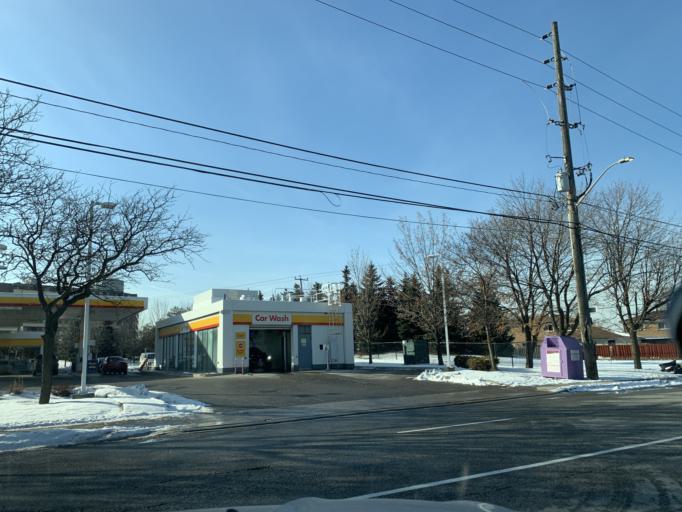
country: CA
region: Ontario
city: Etobicoke
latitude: 43.7166
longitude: -79.6275
